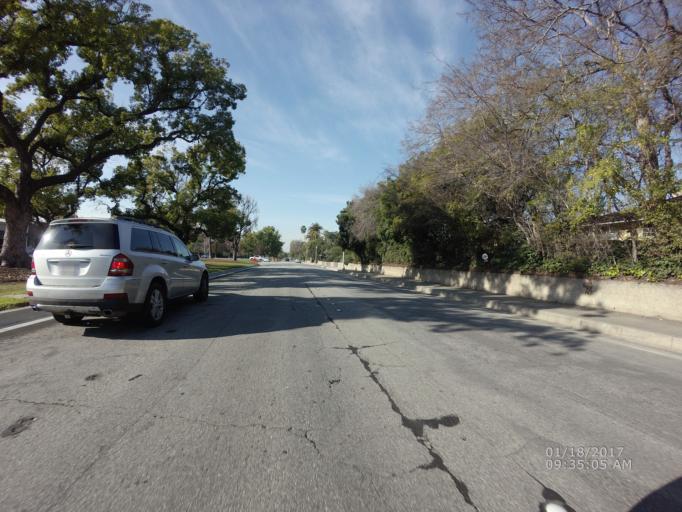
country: US
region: California
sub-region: Los Angeles County
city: San Marino
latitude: 34.1209
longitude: -118.1092
